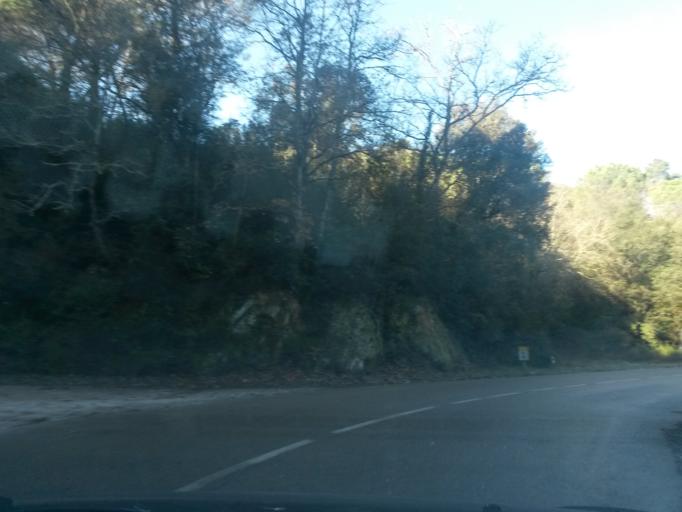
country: ES
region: Catalonia
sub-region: Provincia de Girona
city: Angles
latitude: 41.9931
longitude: 2.6763
